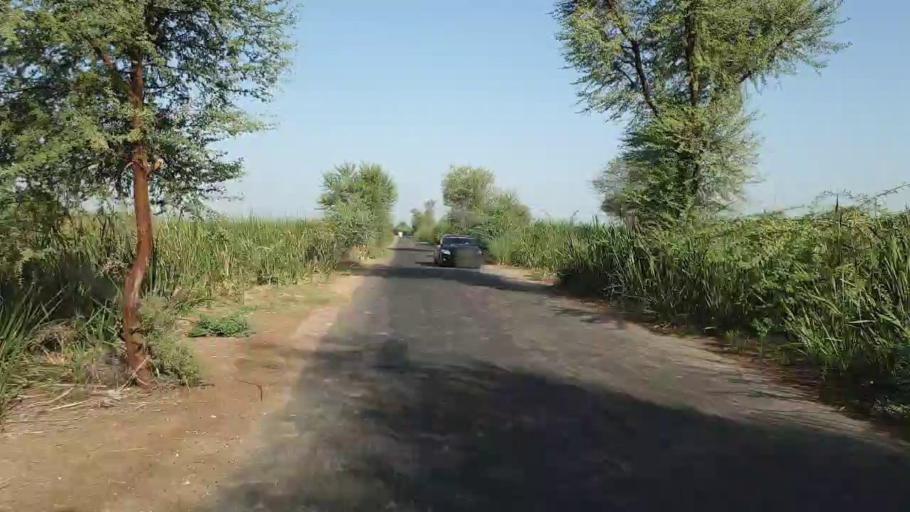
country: PK
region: Sindh
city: Nawabshah
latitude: 26.3773
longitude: 68.4616
